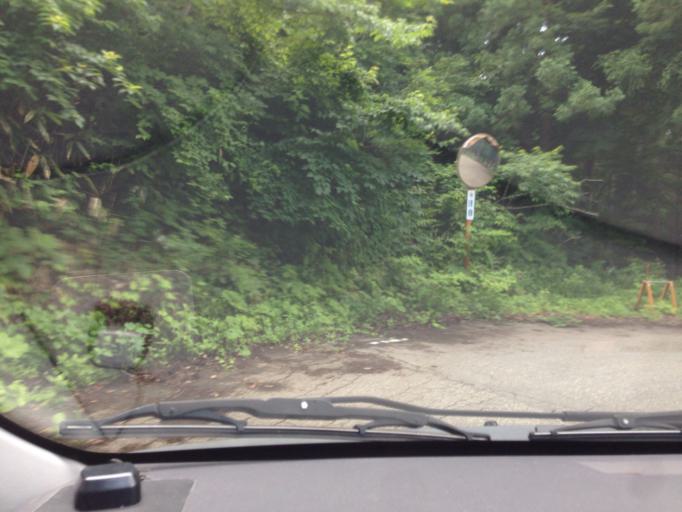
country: JP
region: Fukushima
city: Kitakata
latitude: 37.2806
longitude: 139.8493
